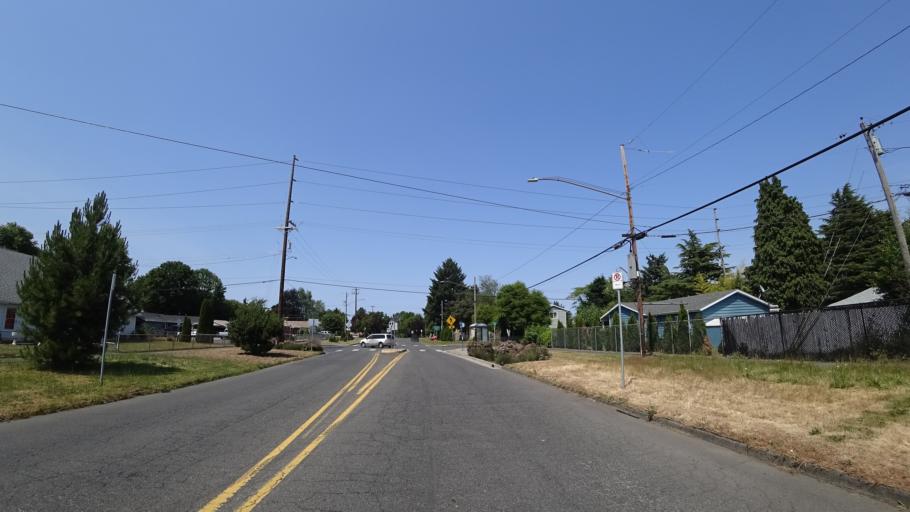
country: US
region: Washington
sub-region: Clark County
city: Vancouver
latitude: 45.5874
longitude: -122.7054
